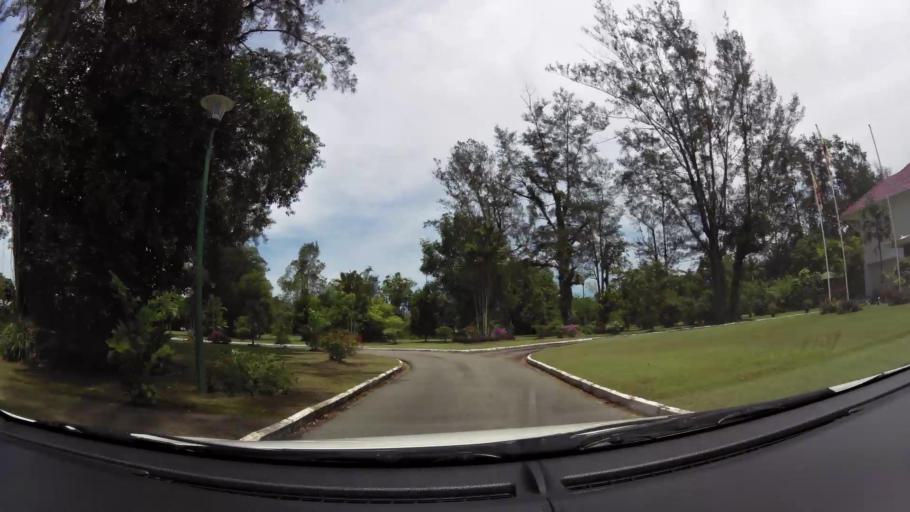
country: BN
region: Belait
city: Kuala Belait
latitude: 4.6018
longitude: 114.2732
